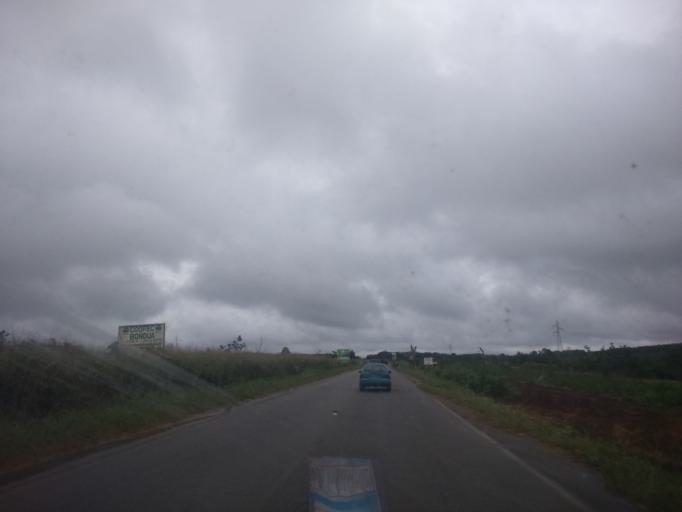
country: CI
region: Sud-Comoe
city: Bonoua
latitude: 5.2757
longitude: -3.5703
